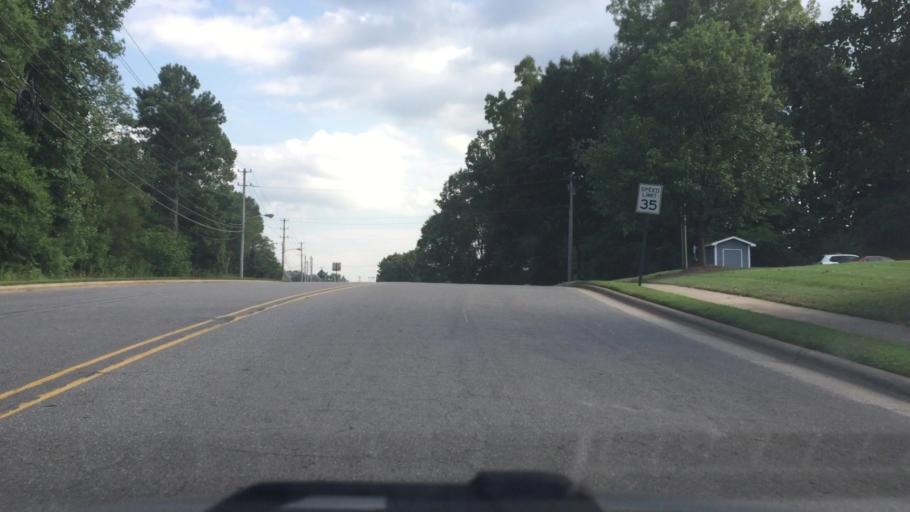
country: US
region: North Carolina
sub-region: Iredell County
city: Statesville
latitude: 35.7983
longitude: -80.8547
